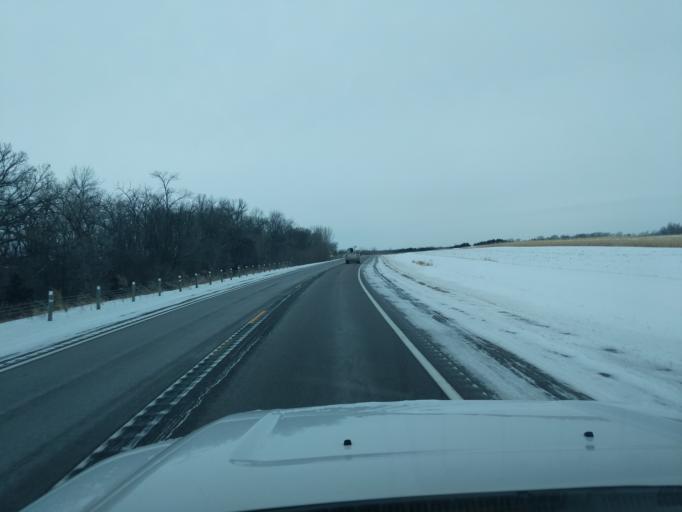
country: US
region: Minnesota
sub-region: Redwood County
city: Redwood Falls
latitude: 44.5668
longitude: -94.9953
